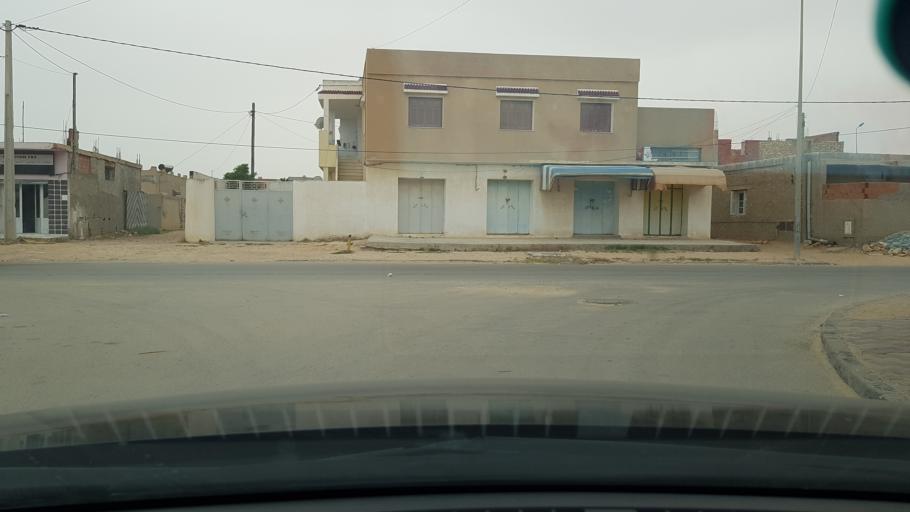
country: TN
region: Safaqis
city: Al Qarmadah
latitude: 34.8270
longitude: 10.7524
